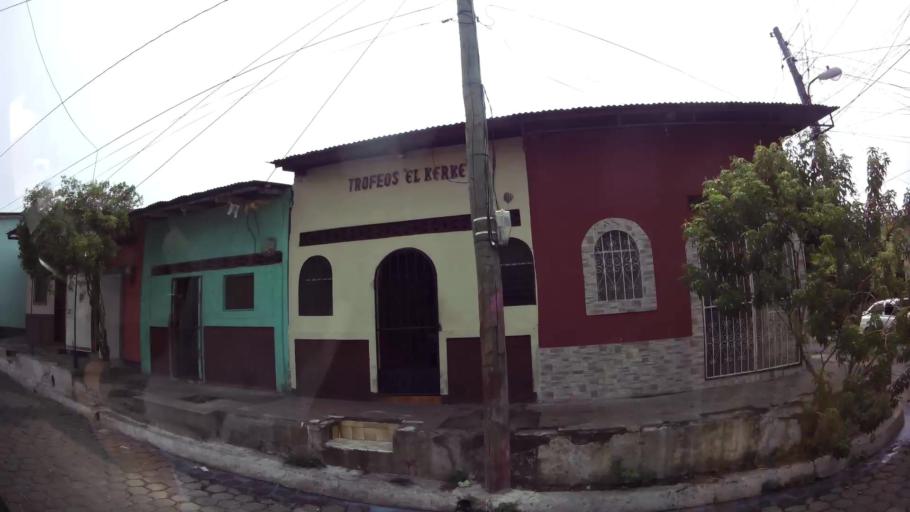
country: NI
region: Chinandega
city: Chinandega
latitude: 12.6342
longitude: -87.1292
